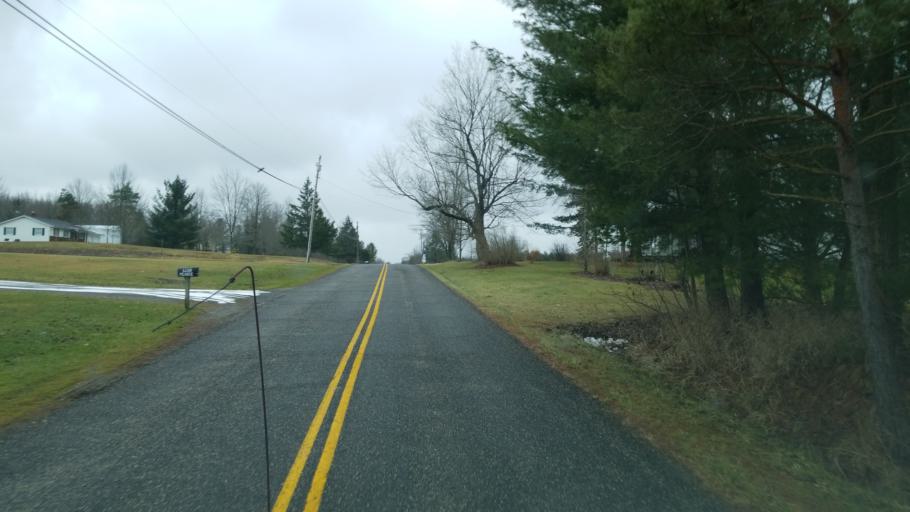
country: US
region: Ohio
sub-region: Portage County
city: Windham
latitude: 41.3377
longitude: -80.9835
